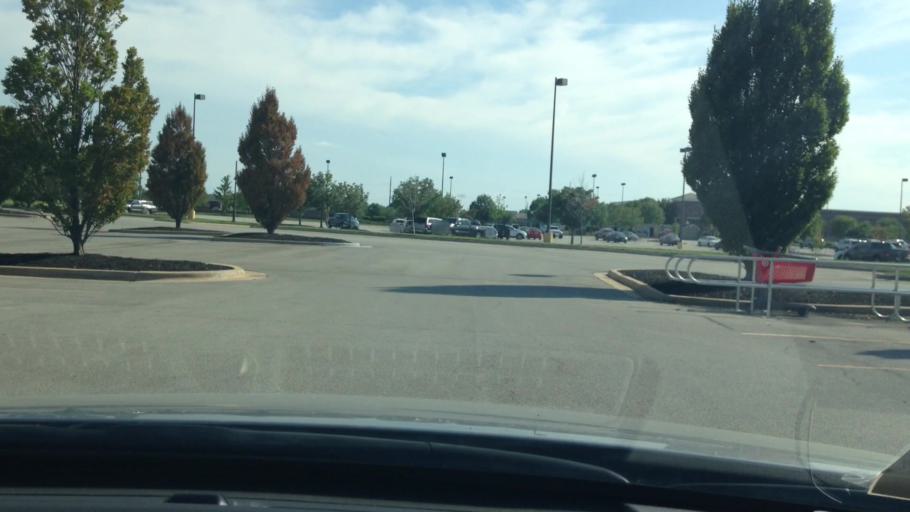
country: US
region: Missouri
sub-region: Jackson County
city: Lees Summit
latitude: 38.9305
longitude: -94.4099
